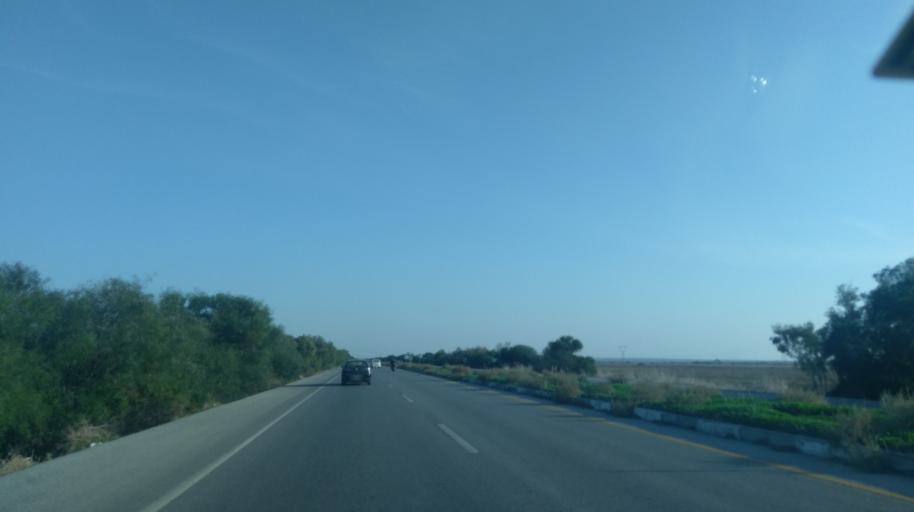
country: CY
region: Ammochostos
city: Acheritou
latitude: 35.1516
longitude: 33.8487
